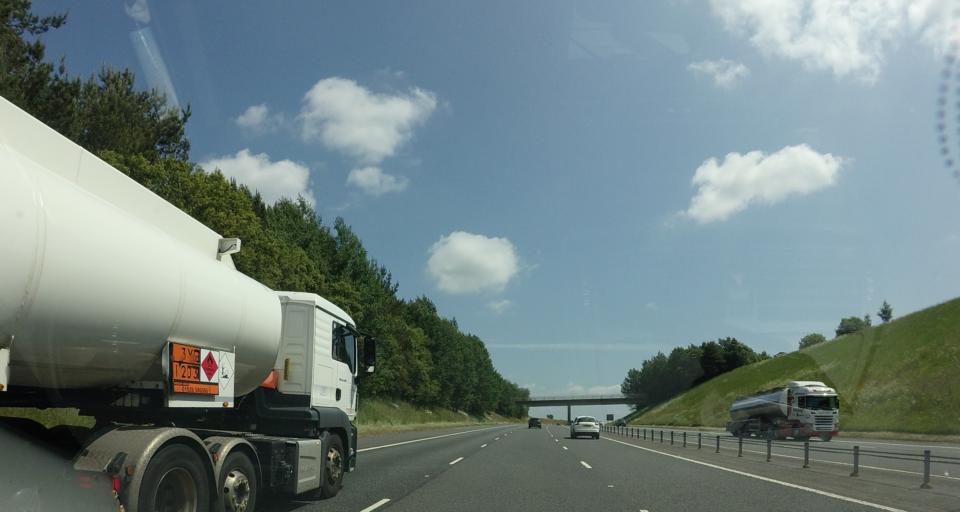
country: GB
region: Scotland
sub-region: Dumfries and Galloway
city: Annan
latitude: 55.0557
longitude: -3.2393
